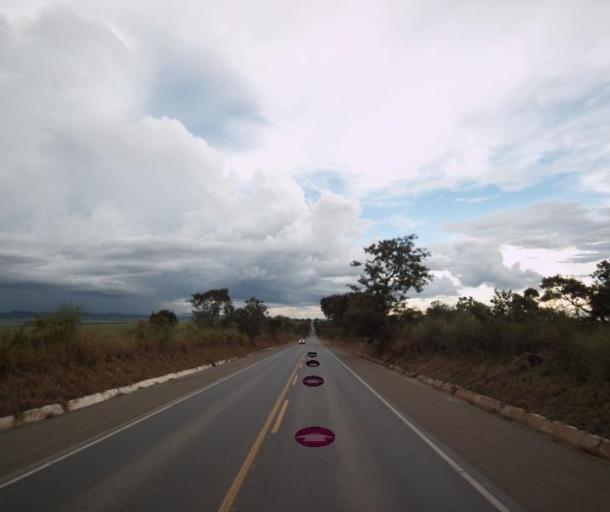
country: BR
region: Goias
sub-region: Itapaci
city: Itapaci
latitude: -14.8521
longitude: -49.3177
